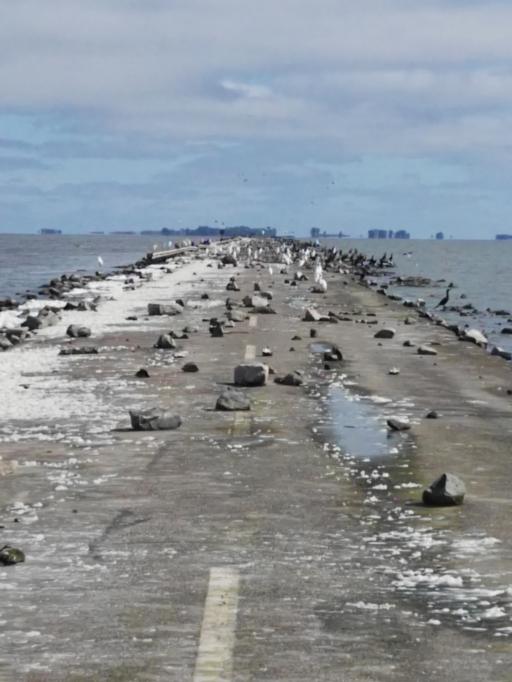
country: AR
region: Santa Fe
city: Rufino
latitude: -34.3838
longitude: -62.2720
